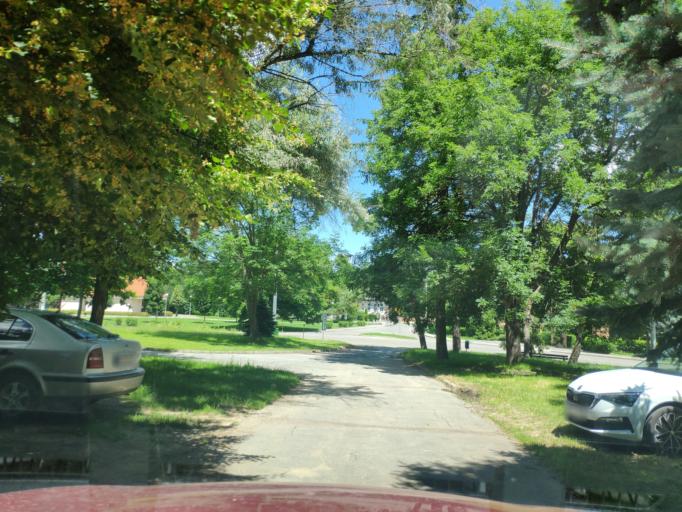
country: HU
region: Borsod-Abauj-Zemplen
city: Ozd
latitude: 48.3121
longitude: 20.2819
